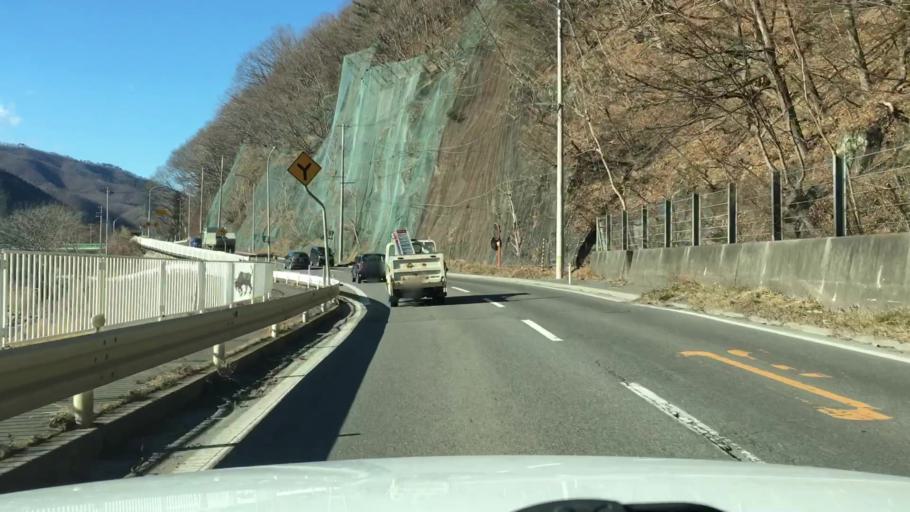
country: JP
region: Iwate
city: Miyako
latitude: 39.6199
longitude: 141.8057
